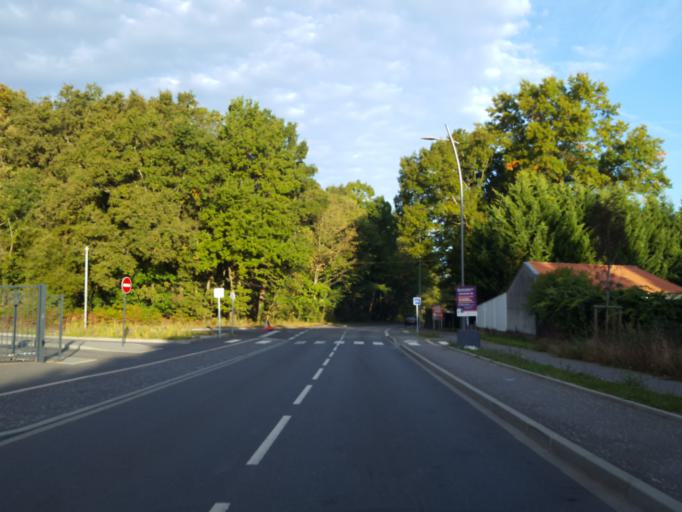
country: FR
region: Pays de la Loire
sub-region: Departement de la Loire-Atlantique
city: Vertou
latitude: 47.1901
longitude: -1.4730
